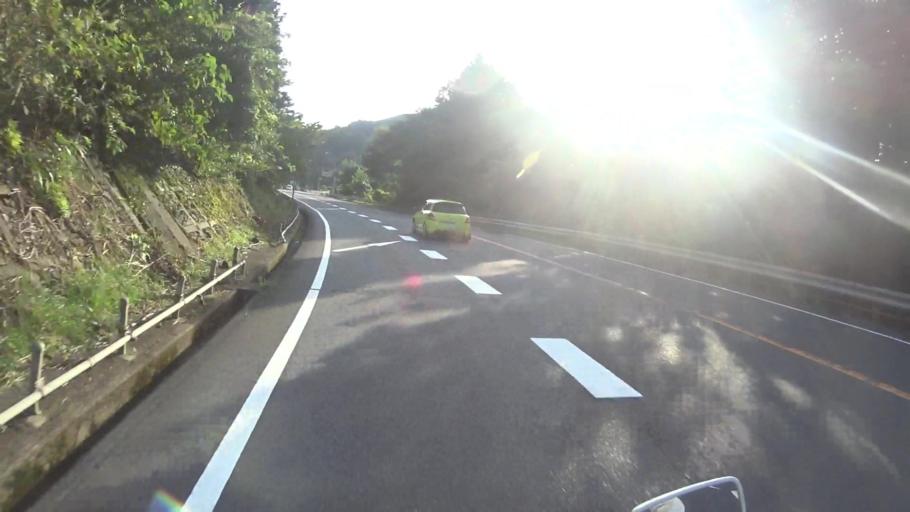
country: JP
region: Kyoto
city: Miyazu
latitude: 35.4514
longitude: 135.0766
